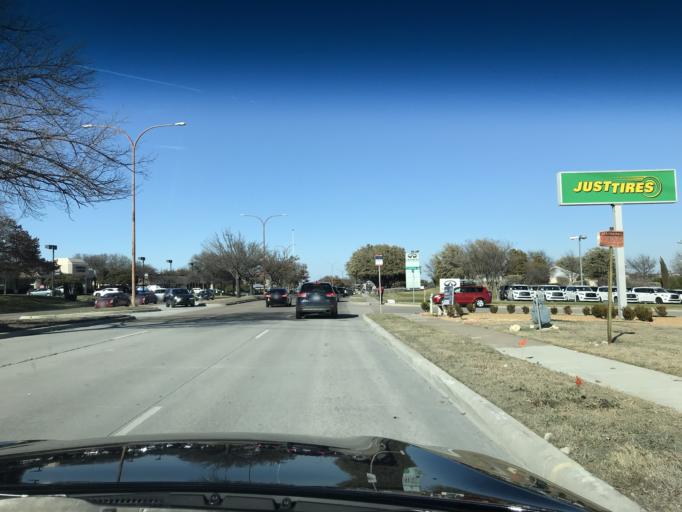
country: US
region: Texas
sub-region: Tarrant County
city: Benbrook
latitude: 32.6745
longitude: -97.4181
